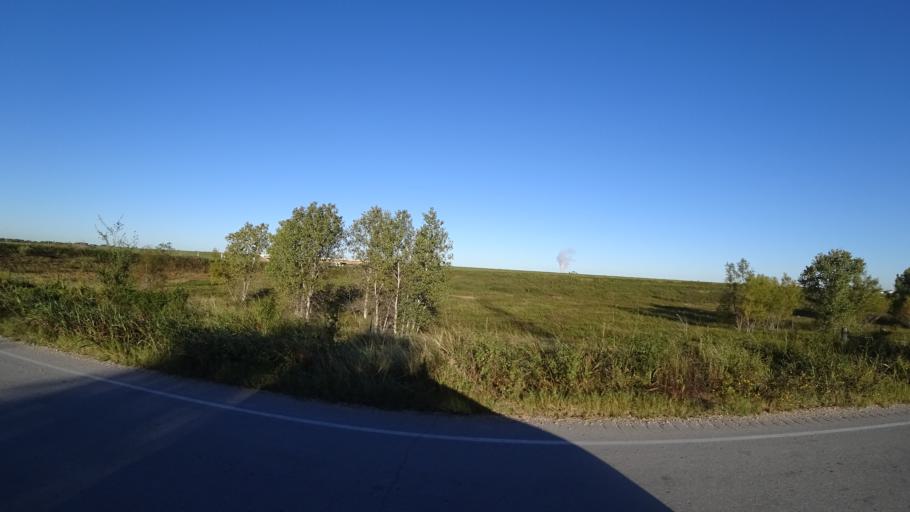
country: US
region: Texas
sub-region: Travis County
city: Hornsby Bend
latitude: 30.2285
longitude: -97.6169
